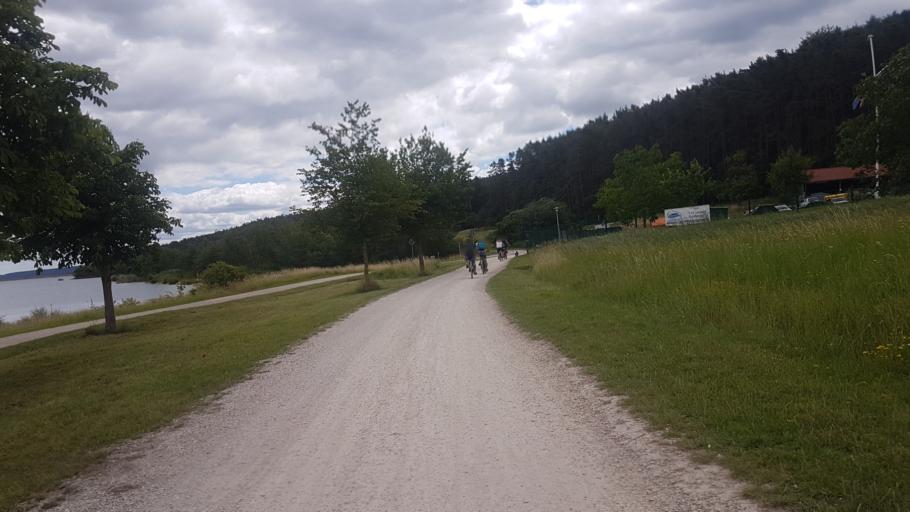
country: DE
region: Bavaria
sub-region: Regierungsbezirk Mittelfranken
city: Pleinfeld
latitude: 49.1198
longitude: 10.9426
